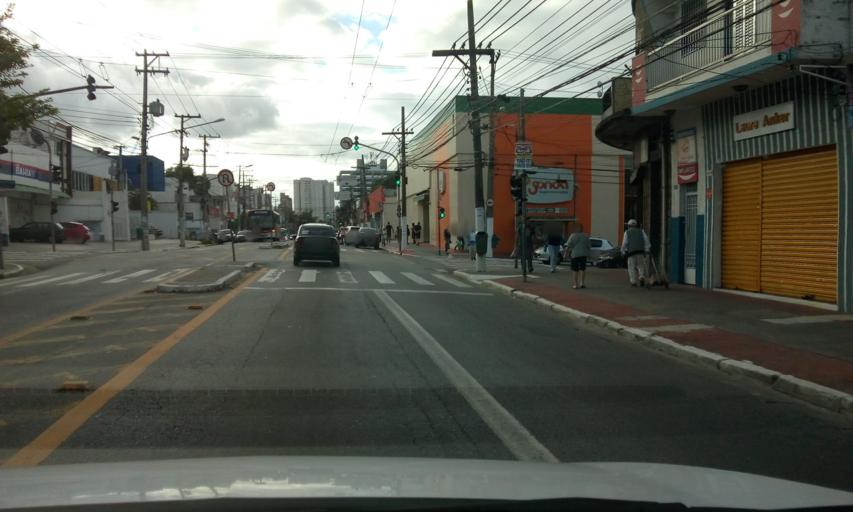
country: BR
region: Sao Paulo
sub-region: Sao Caetano Do Sul
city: Sao Caetano do Sul
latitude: -23.5480
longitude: -46.5389
